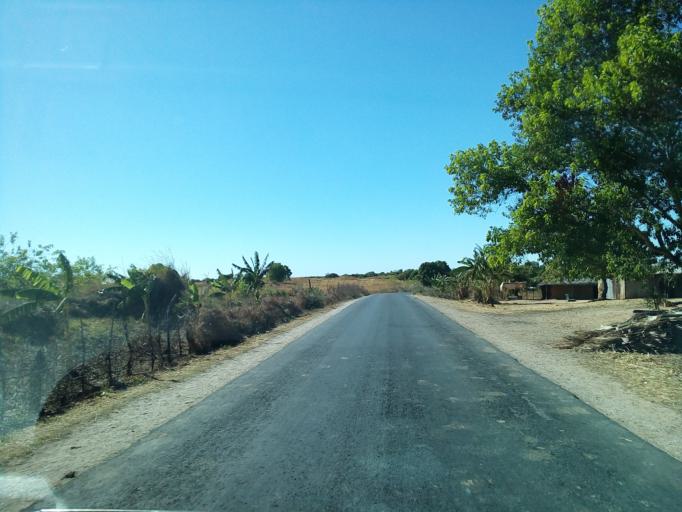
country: MG
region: Boeny
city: Marovoay
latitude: -15.9875
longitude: 46.6859
